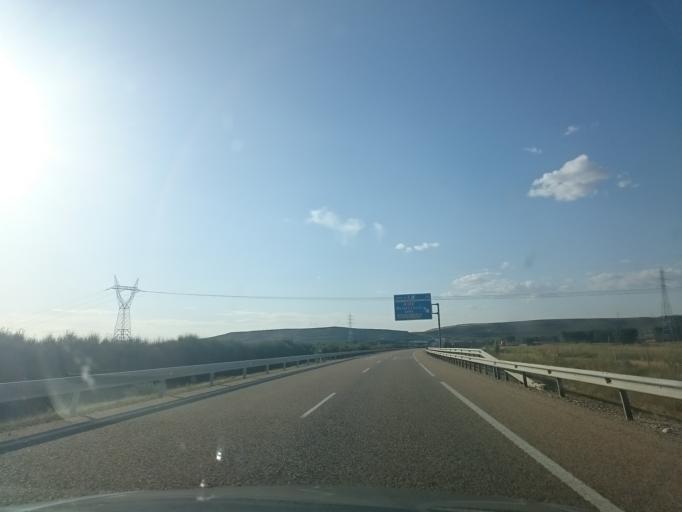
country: ES
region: Castille and Leon
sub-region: Provincia de Burgos
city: San Mames de Burgos
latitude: 42.3389
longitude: -3.7873
